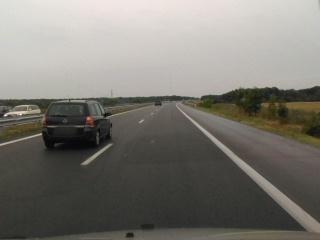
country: BG
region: Stara Zagora
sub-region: Obshtina Stara Zagora
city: Stara Zagora
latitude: 42.3585
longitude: 25.7516
